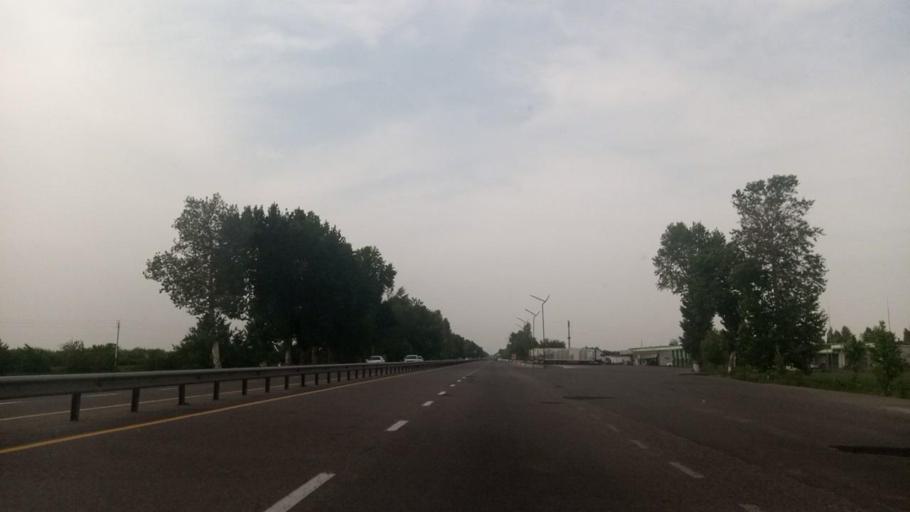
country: UZ
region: Toshkent Shahri
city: Bektemir
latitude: 41.2064
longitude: 69.4029
